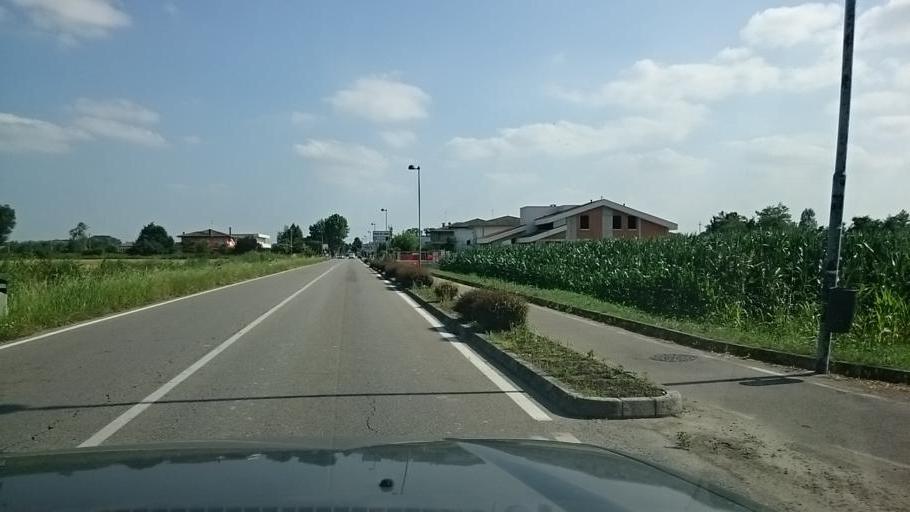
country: IT
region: Veneto
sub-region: Provincia di Padova
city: Villa del Conte
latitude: 45.5954
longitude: 11.8568
